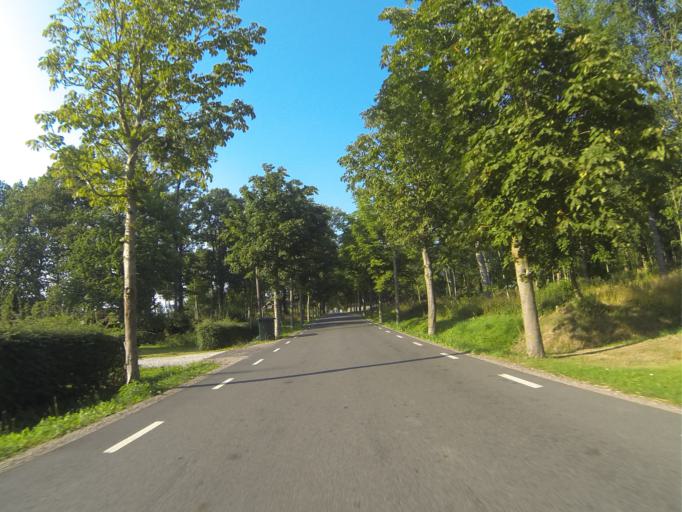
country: SE
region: Skane
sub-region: Lunds Kommun
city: Genarp
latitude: 55.6241
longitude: 13.4063
